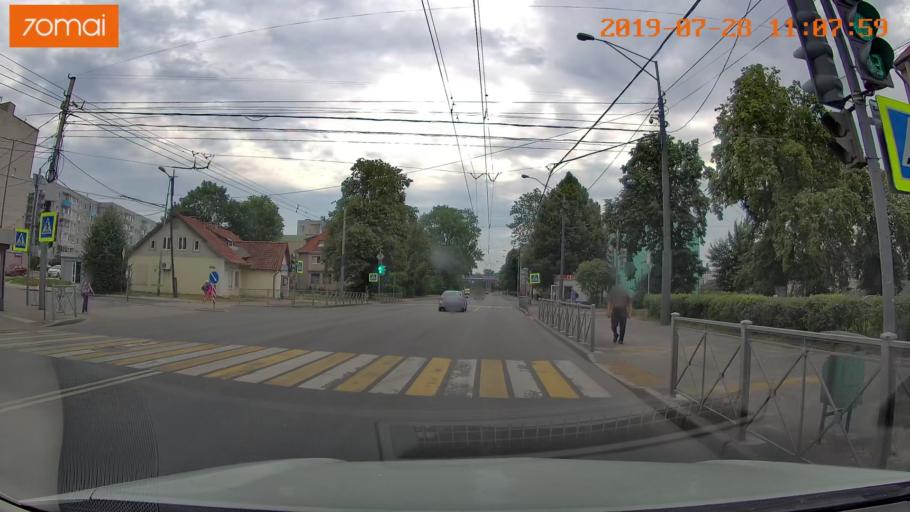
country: RU
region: Kaliningrad
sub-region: Gorod Kaliningrad
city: Kaliningrad
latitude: 54.7116
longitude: 20.4363
